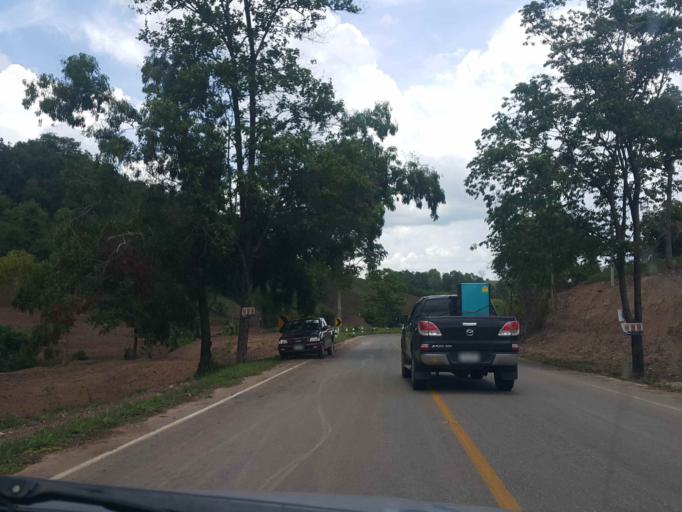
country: TH
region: Phayao
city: Chiang Muan
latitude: 18.9003
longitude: 100.1322
